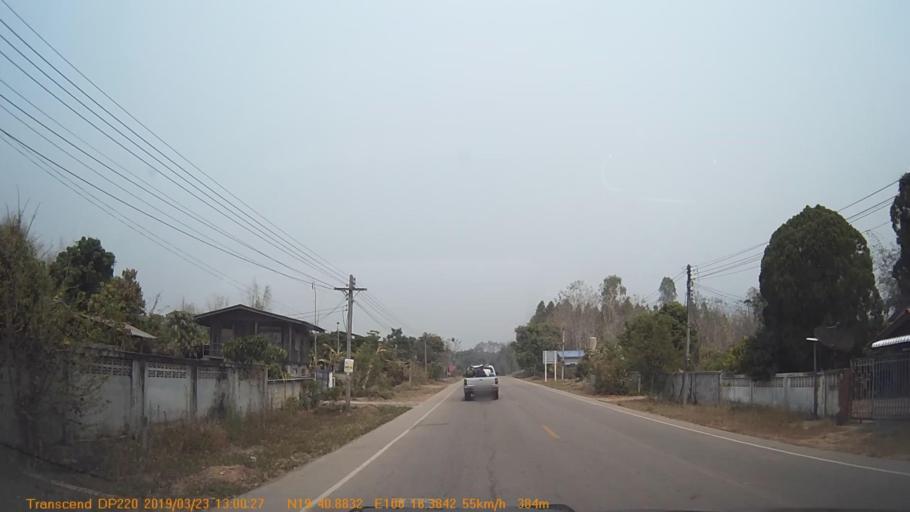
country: TH
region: Chiang Rai
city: Thoeng
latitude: 19.6815
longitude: 100.2732
